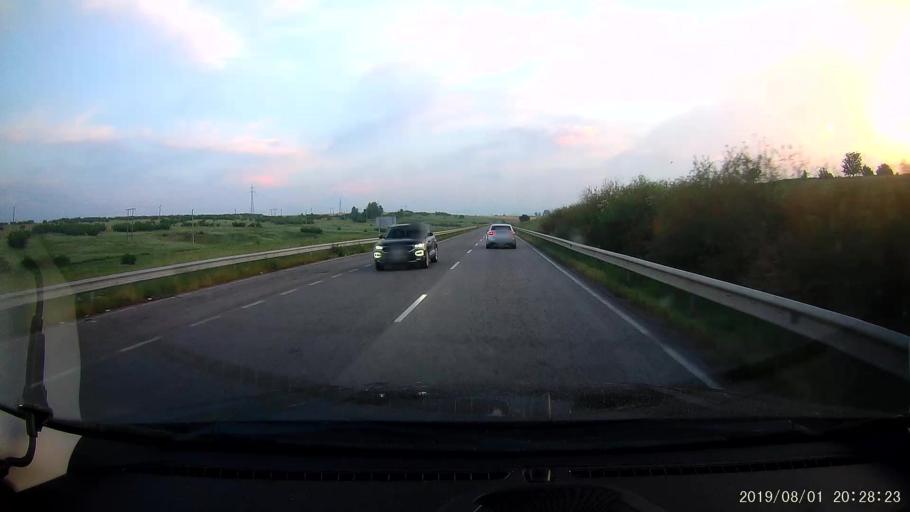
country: BG
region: Yambol
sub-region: Obshtina Elkhovo
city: Elkhovo
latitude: 42.1694
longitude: 26.5784
